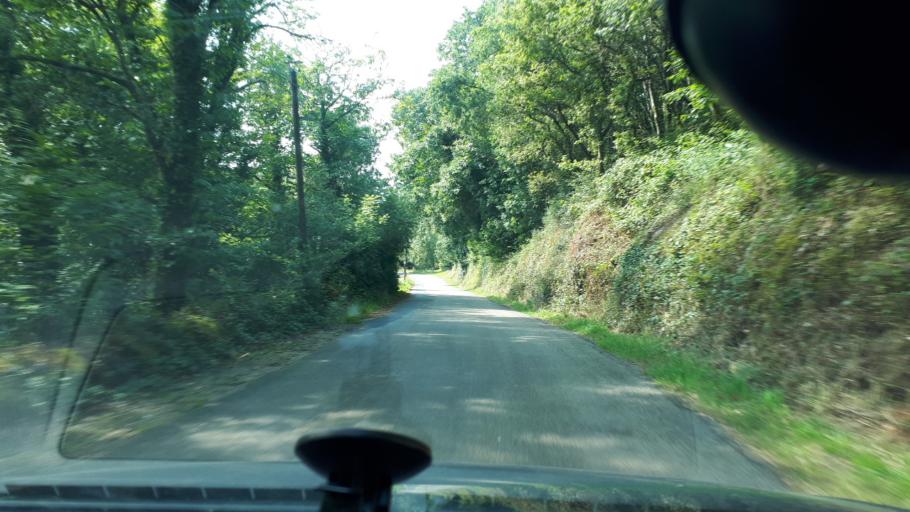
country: FR
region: Brittany
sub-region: Departement du Finistere
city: Pouldreuzic
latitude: 47.9740
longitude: -4.3679
